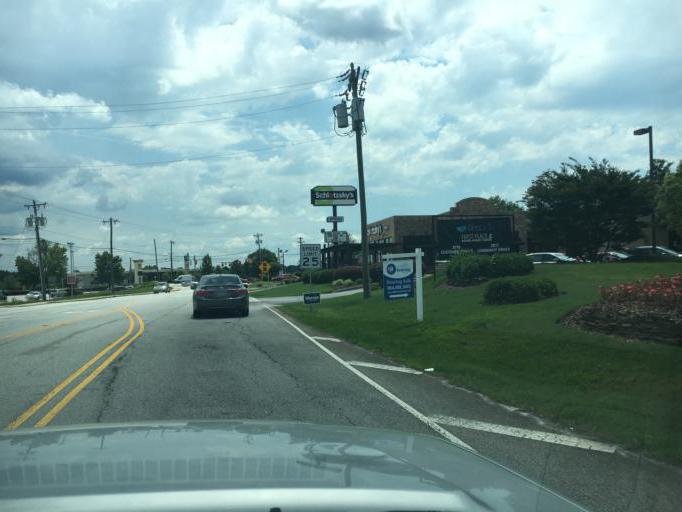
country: US
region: South Carolina
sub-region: Greenville County
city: Taylors
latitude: 34.8612
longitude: -82.2661
